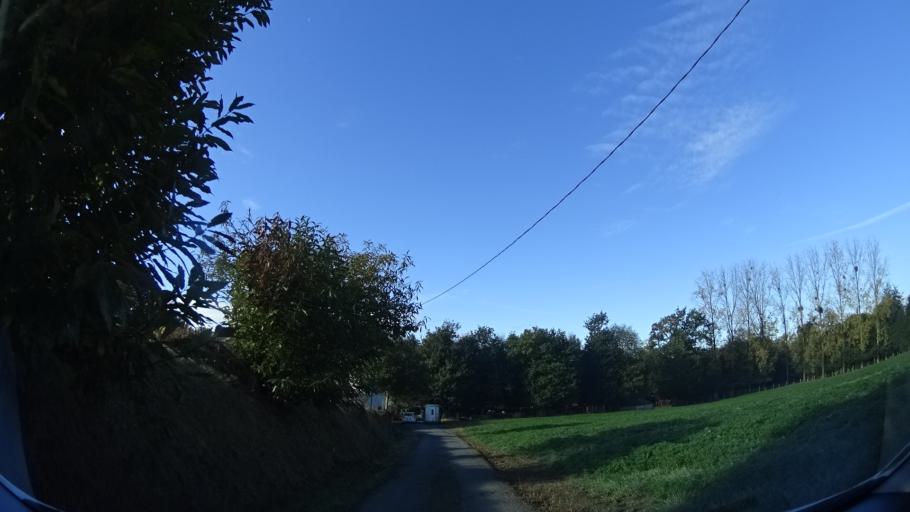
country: FR
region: Brittany
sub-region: Departement d'Ille-et-Vilaine
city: Geveze
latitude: 48.2008
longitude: -1.7830
